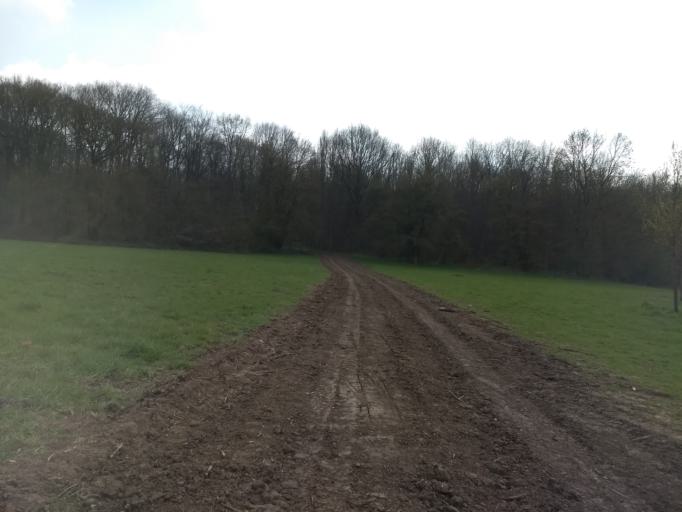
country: FR
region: Nord-Pas-de-Calais
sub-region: Departement du Pas-de-Calais
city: Mont-Saint-Eloi
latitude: 50.3363
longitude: 2.6927
